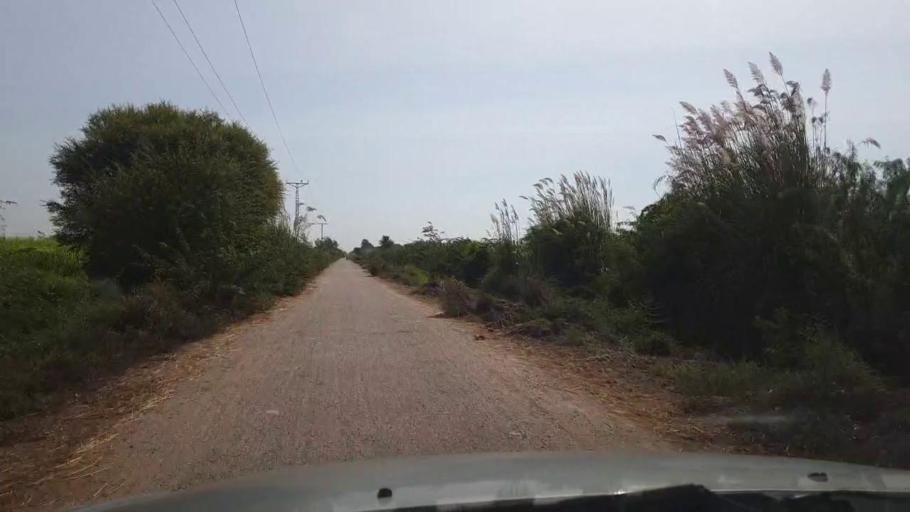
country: PK
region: Sindh
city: Tando Muhammad Khan
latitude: 25.1555
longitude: 68.3807
